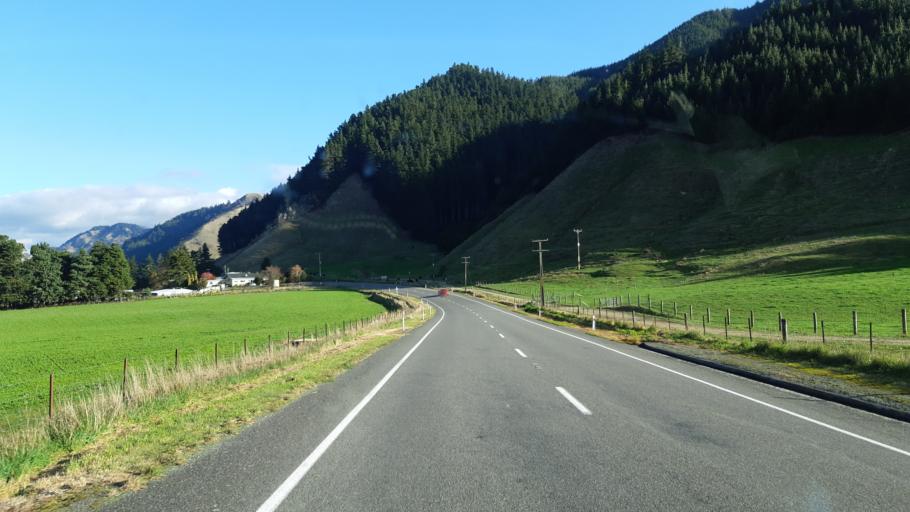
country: NZ
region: Marlborough
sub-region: Marlborough District
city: Picton
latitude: -41.3047
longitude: 173.7696
